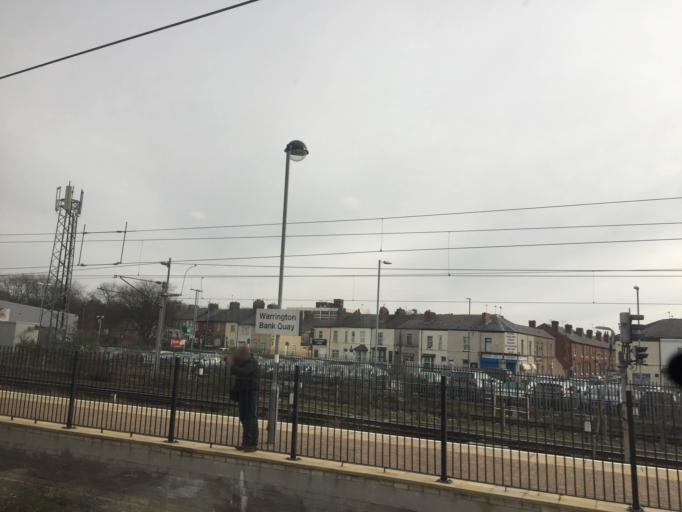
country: GB
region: England
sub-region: Warrington
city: Warrington
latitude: 53.3867
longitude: -2.6033
